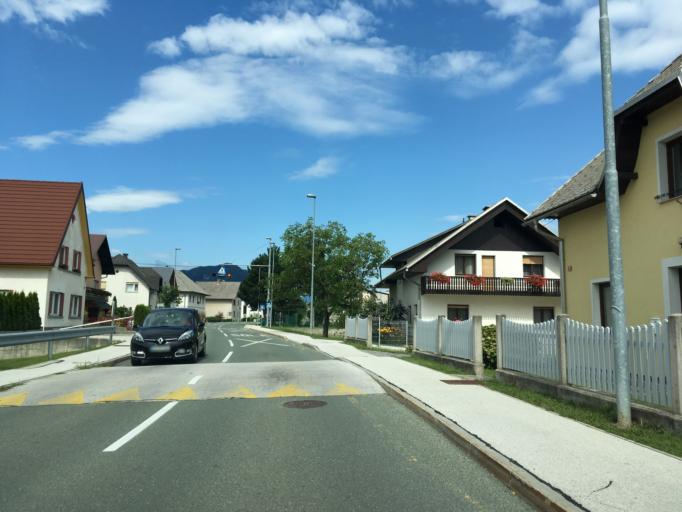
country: SI
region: Zirovnica
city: Zirovnica
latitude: 46.3979
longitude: 14.1462
